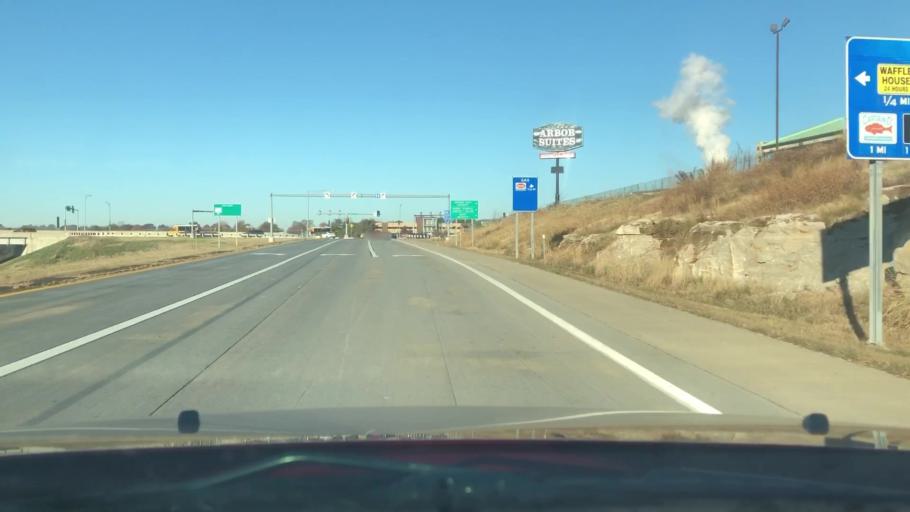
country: US
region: Missouri
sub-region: Greene County
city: Springfield
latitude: 37.1426
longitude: -93.2759
